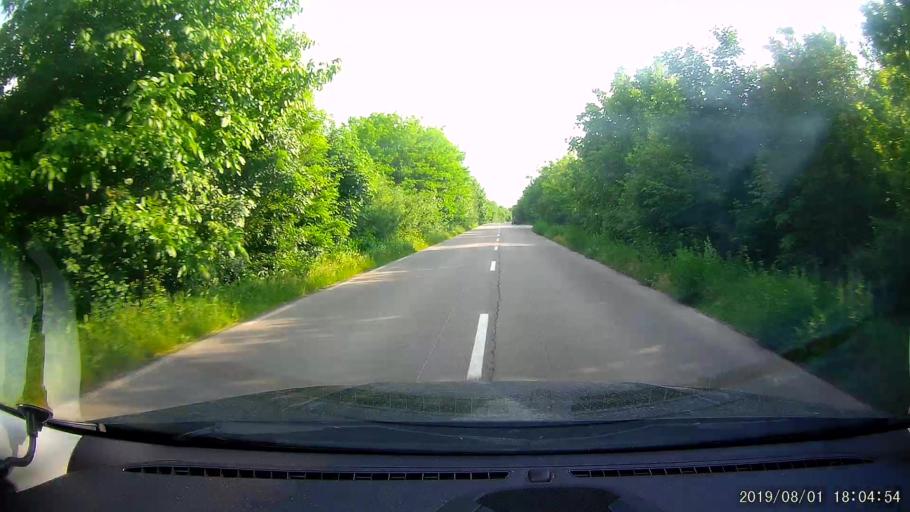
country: BG
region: Silistra
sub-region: Obshtina Alfatar
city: Alfatar
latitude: 43.9005
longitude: 27.2707
